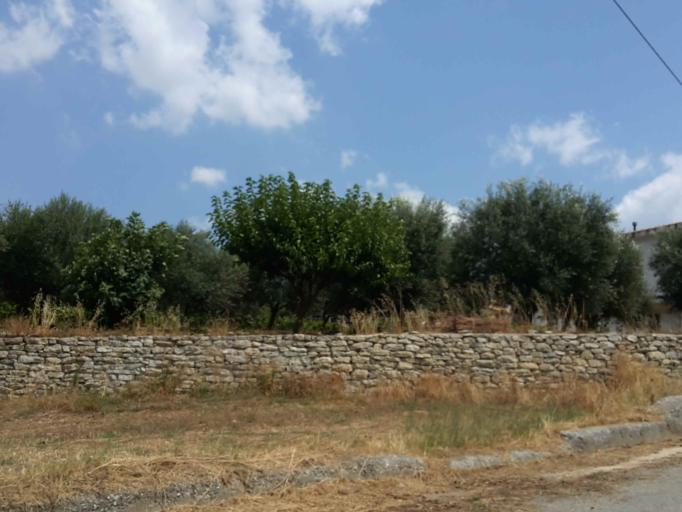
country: IT
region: Calabria
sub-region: Provincia di Reggio Calabria
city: Condofuri
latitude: 37.9860
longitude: 15.8445
